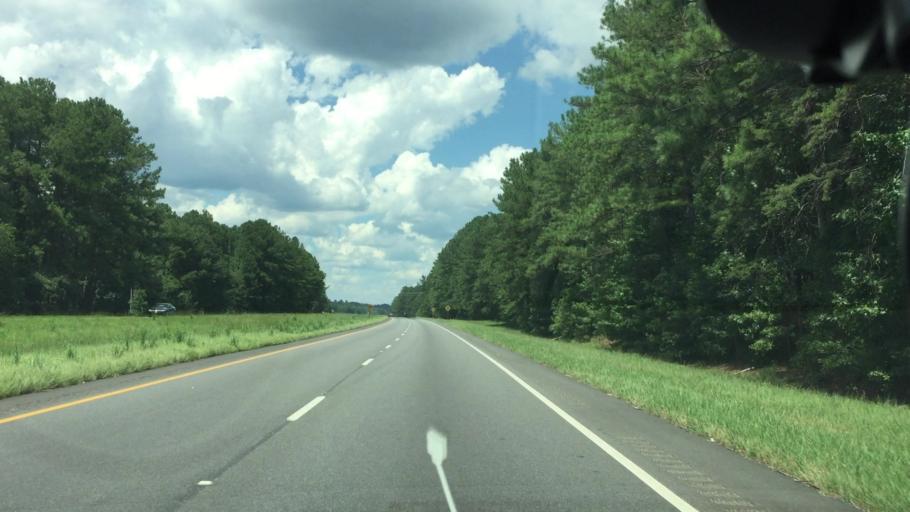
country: US
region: Alabama
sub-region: Pike County
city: Troy
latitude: 31.9120
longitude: -86.0127
